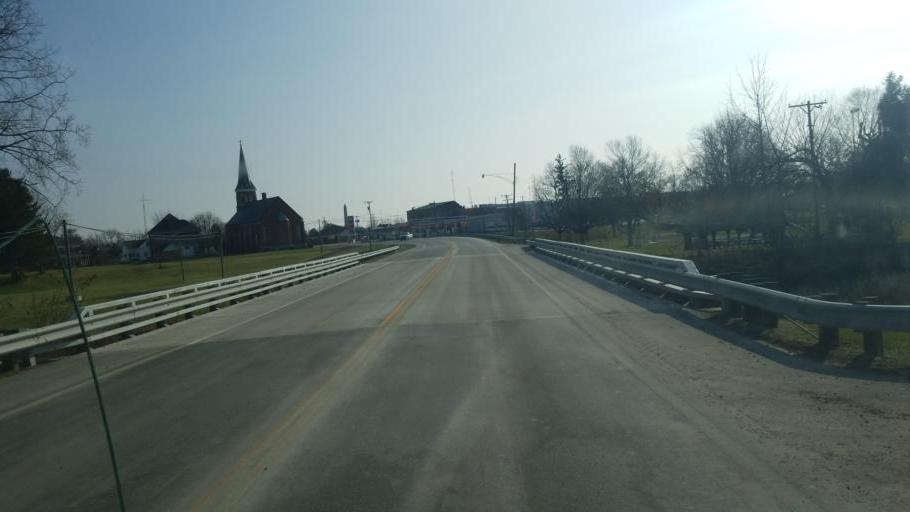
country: US
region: Ohio
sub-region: Mercer County
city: Fort Recovery
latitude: 40.4163
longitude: -84.7818
